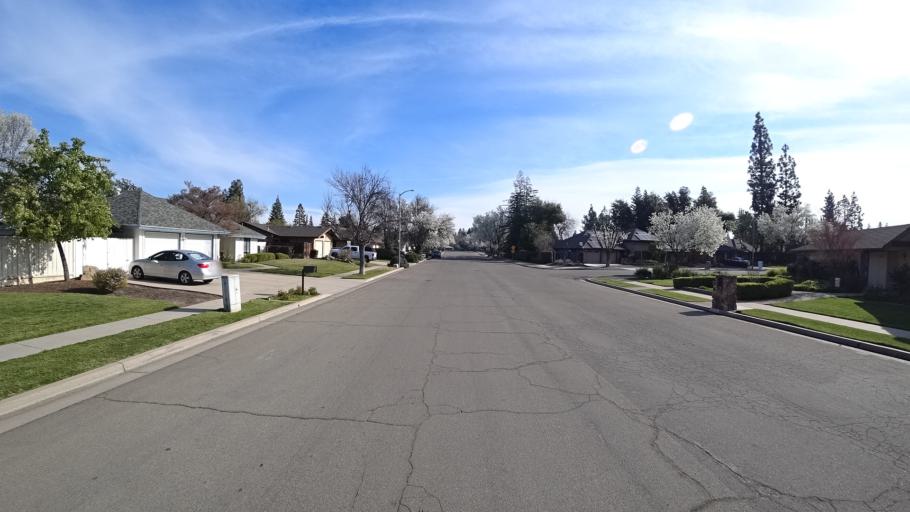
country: US
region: California
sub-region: Fresno County
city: Clovis
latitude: 36.8627
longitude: -119.7775
